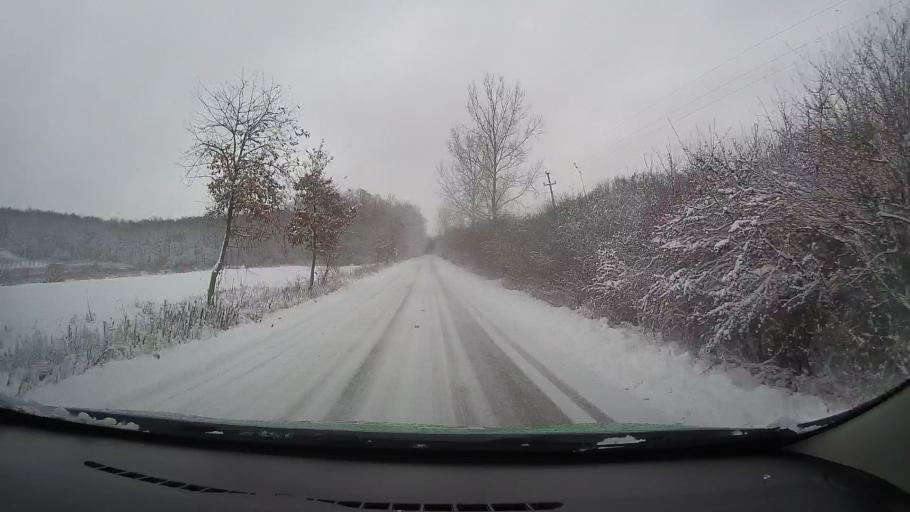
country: RO
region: Hunedoara
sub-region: Comuna Pestisu Mic
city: Pestisu Mic
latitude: 45.8146
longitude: 22.8970
